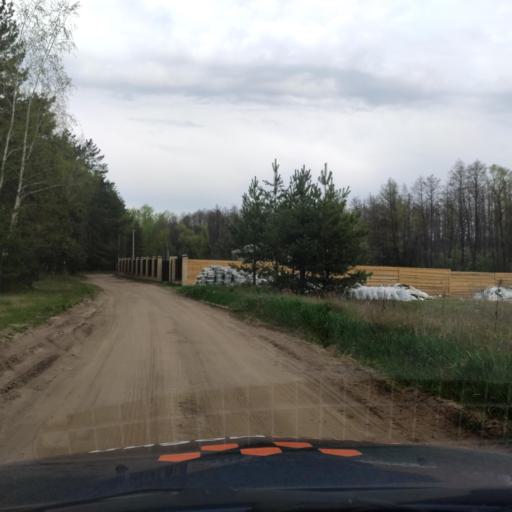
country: RU
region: Voronezj
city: Podgornoye
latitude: 51.8680
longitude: 39.1701
